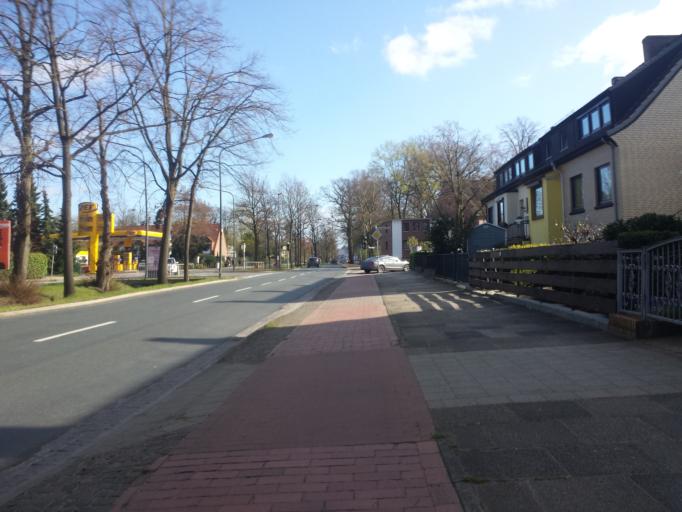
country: DE
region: Lower Saxony
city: Lilienthal
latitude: 53.0751
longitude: 8.8820
